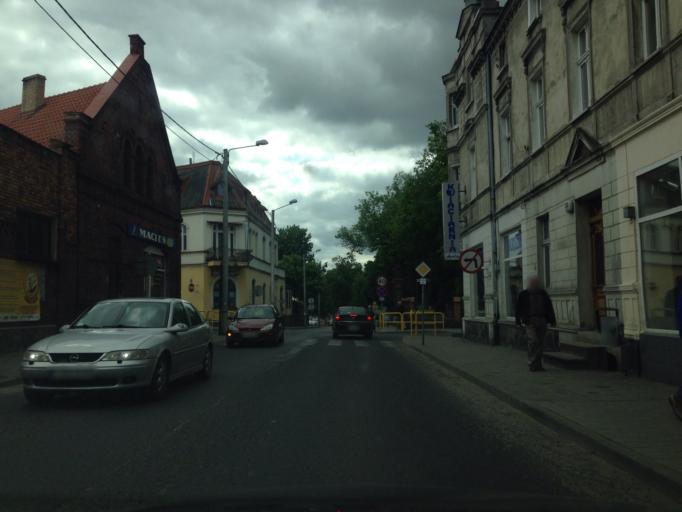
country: PL
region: Kujawsko-Pomorskie
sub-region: Powiat swiecki
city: Swiecie
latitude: 53.4084
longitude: 18.4482
